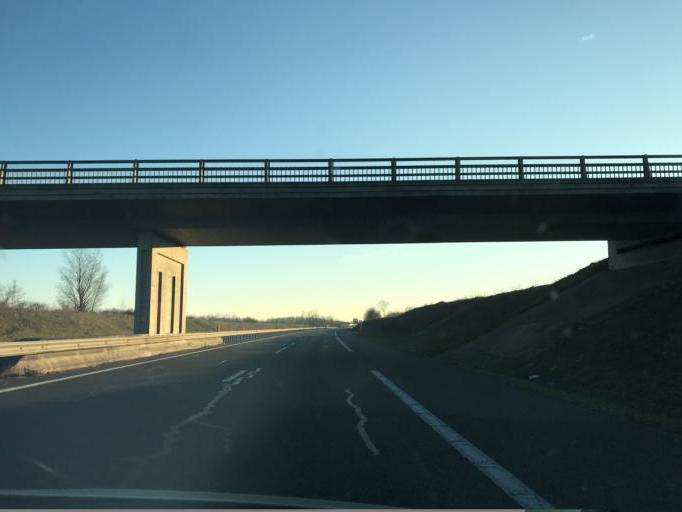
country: FR
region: Bourgogne
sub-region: Departement de l'Yonne
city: Egriselles-le-Bocage
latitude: 48.1538
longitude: 3.1705
